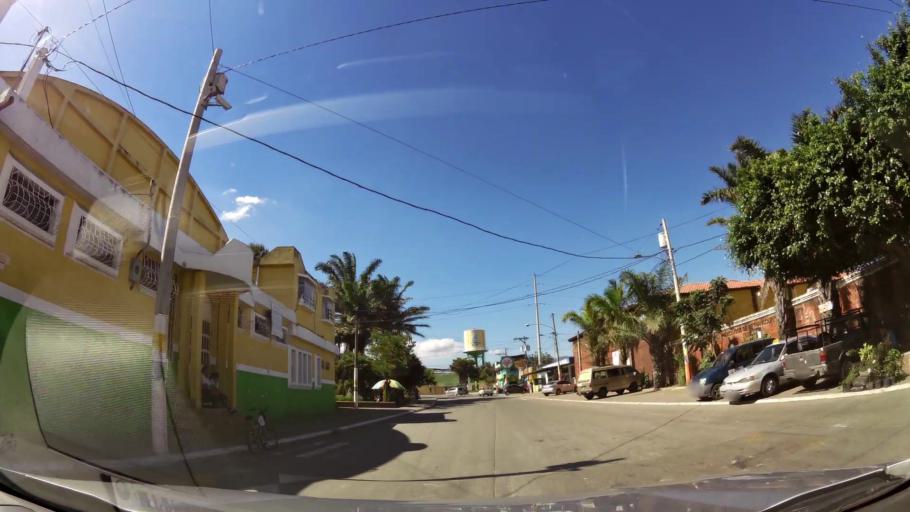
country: GT
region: Guatemala
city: Petapa
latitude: 14.5021
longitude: -90.5608
